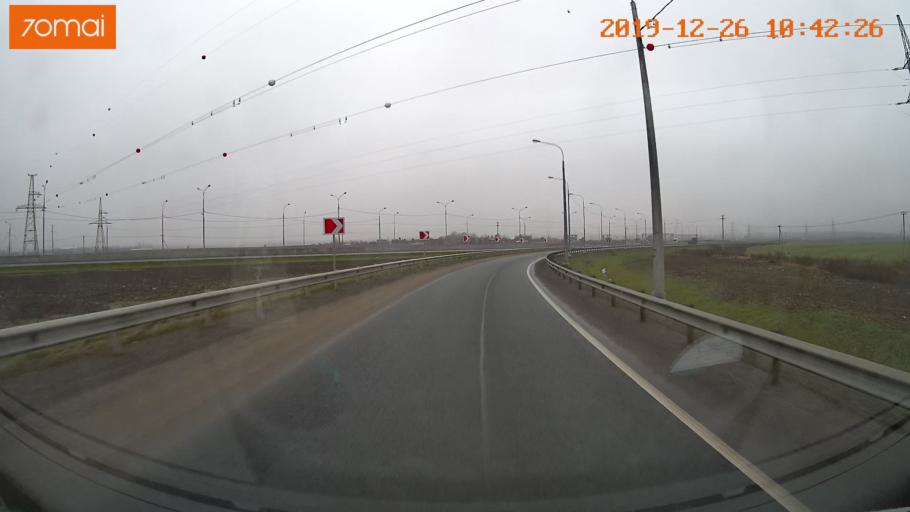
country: RU
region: Vologda
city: Vologda
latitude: 59.1599
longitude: 39.8096
